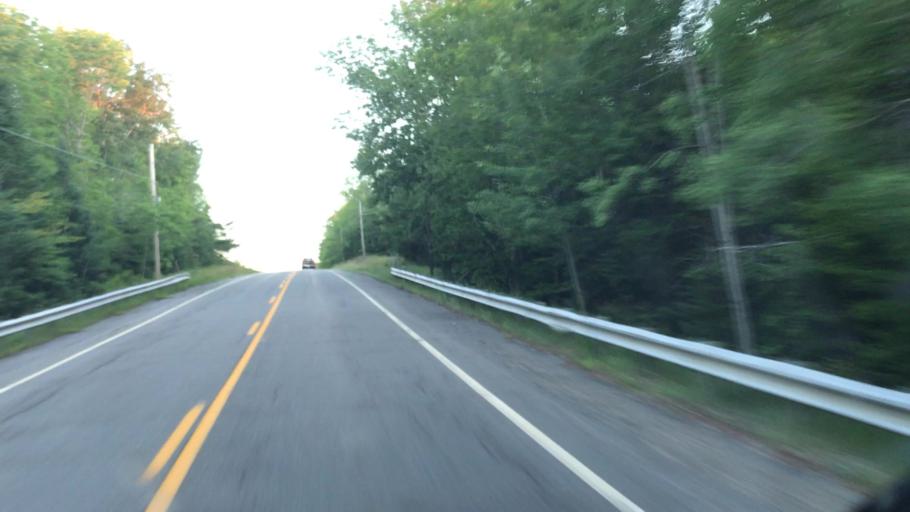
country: US
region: Maine
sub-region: Penobscot County
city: Medway
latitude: 45.5964
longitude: -68.3110
